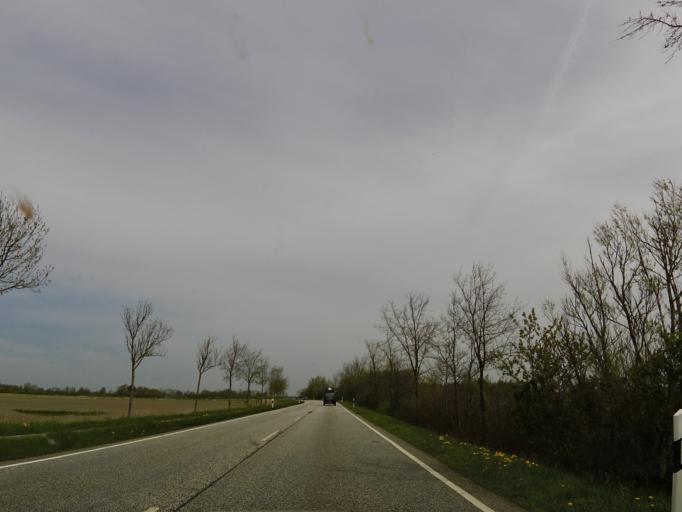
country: DE
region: Schleswig-Holstein
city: Tonning
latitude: 54.3441
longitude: 8.9687
